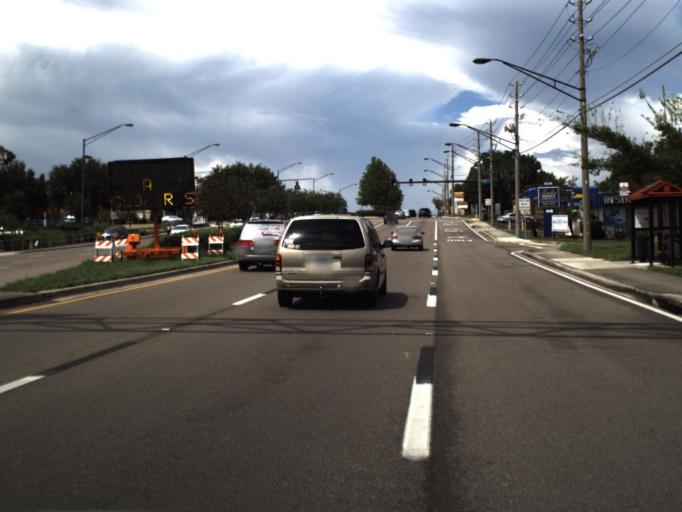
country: US
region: Florida
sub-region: Polk County
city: Medulla
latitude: 27.9977
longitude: -81.9568
